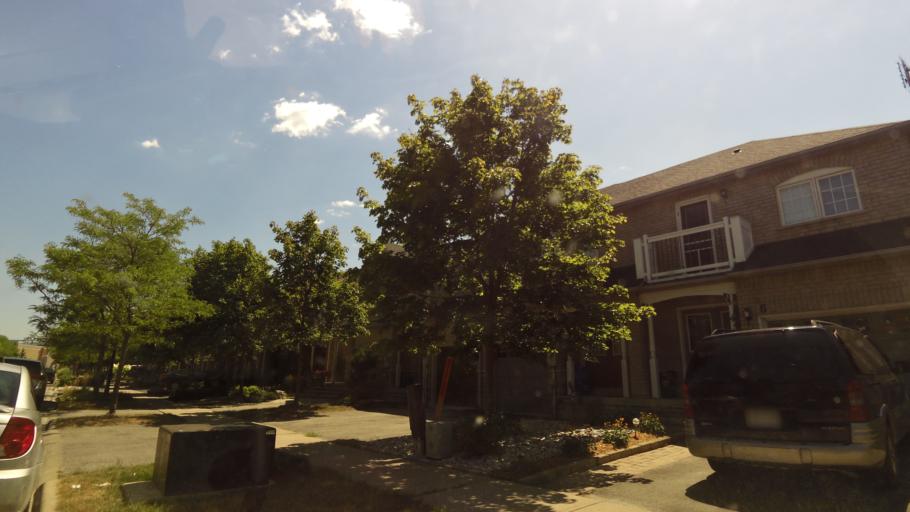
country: CA
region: Ontario
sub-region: Halton
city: Milton
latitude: 43.6531
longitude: -79.9127
